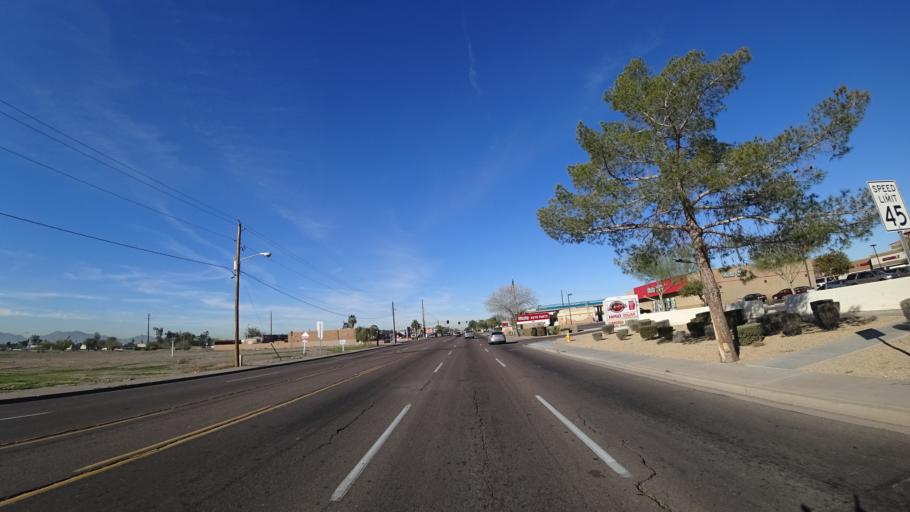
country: US
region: Arizona
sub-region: Maricopa County
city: Glendale
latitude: 33.4660
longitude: -112.1845
